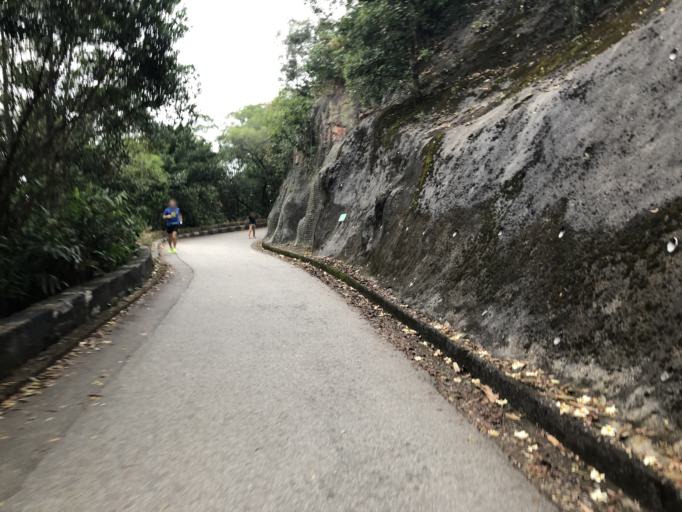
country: HK
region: Wanchai
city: Wan Chai
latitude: 22.2737
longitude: 114.2104
